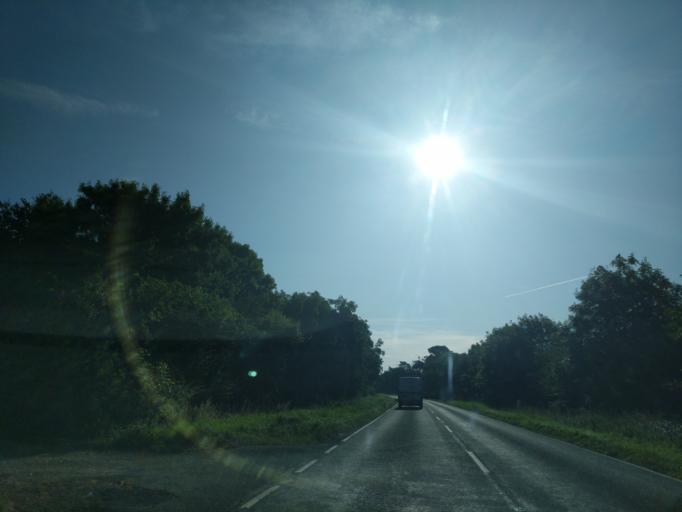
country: GB
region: England
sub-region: District of Rutland
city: Clipsham
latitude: 52.8038
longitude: -0.5952
